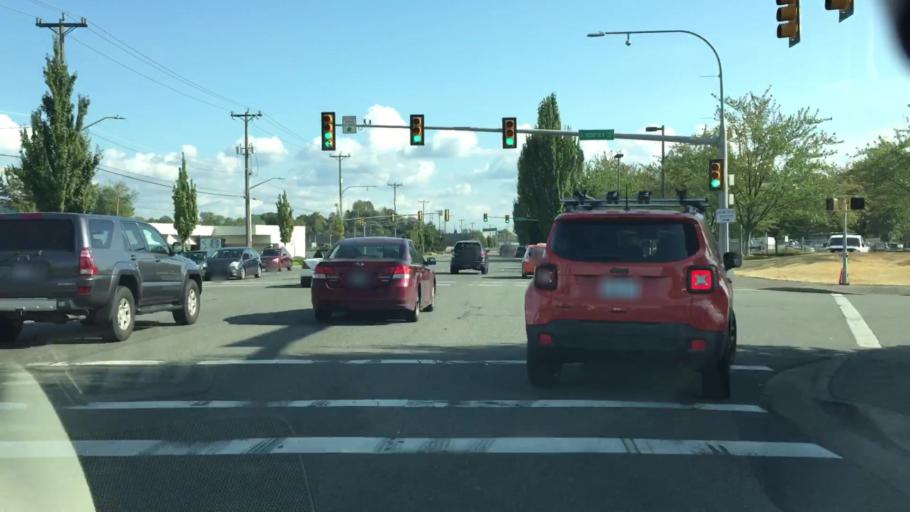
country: US
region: Washington
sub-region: King County
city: Riverton
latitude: 47.5127
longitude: -122.2943
